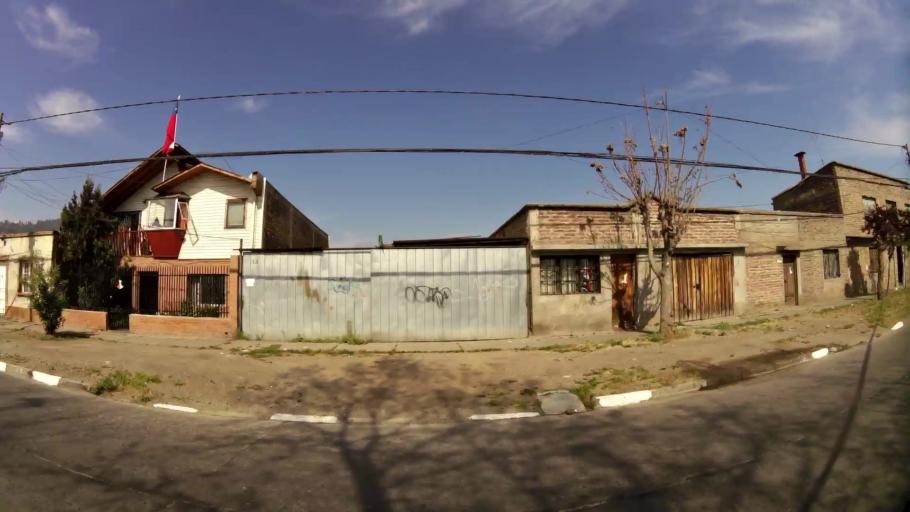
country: CL
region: Santiago Metropolitan
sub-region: Provincia de Santiago
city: Santiago
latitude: -33.4028
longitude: -70.6277
